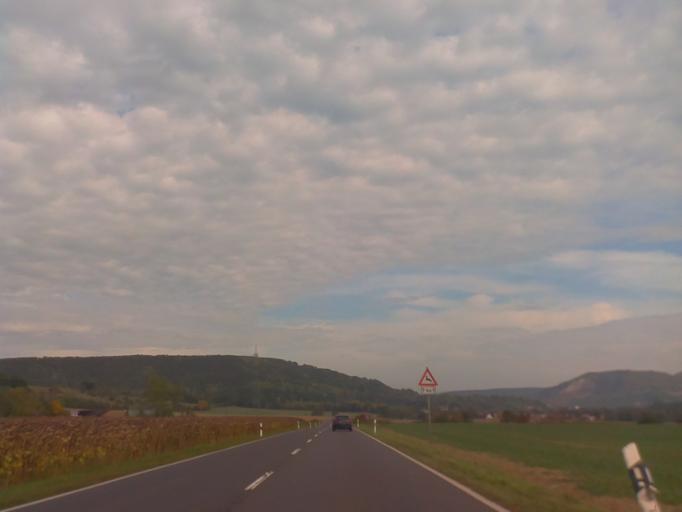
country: DE
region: Thuringia
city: Freienorla
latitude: 50.7792
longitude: 11.5500
